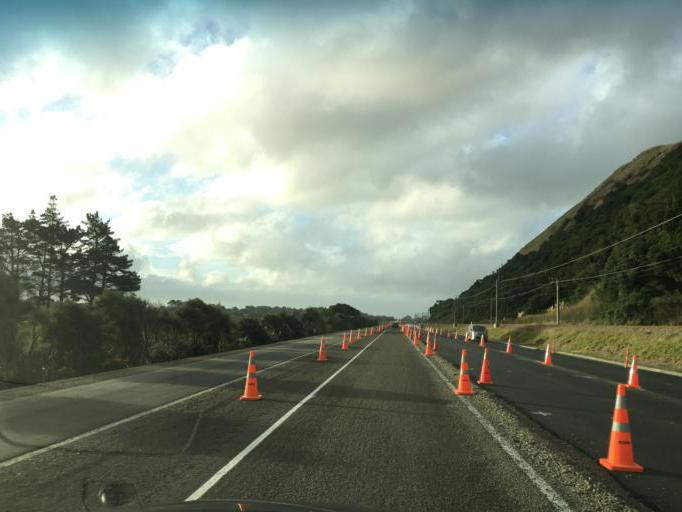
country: NZ
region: Wellington
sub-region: Kapiti Coast District
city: Paraparaumu
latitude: -40.9491
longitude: 174.9899
